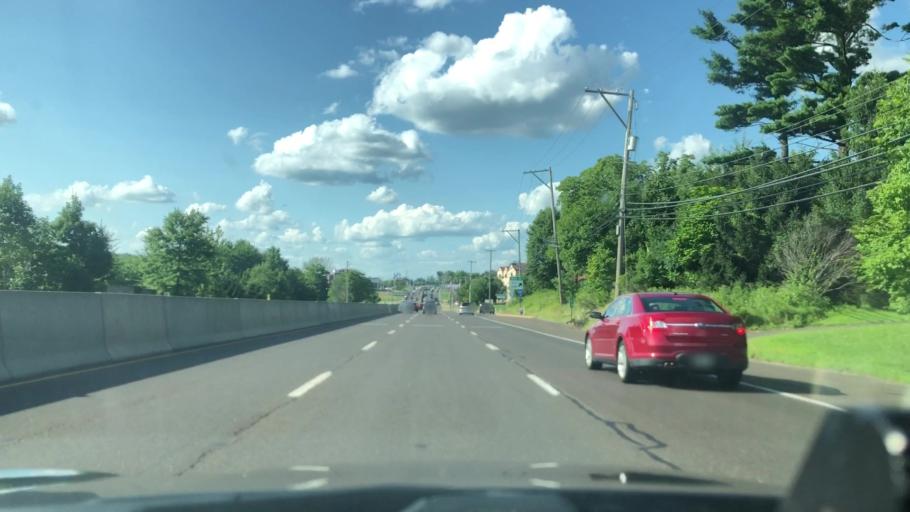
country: US
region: Pennsylvania
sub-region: Montgomery County
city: Spring House
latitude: 40.2021
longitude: -75.2242
